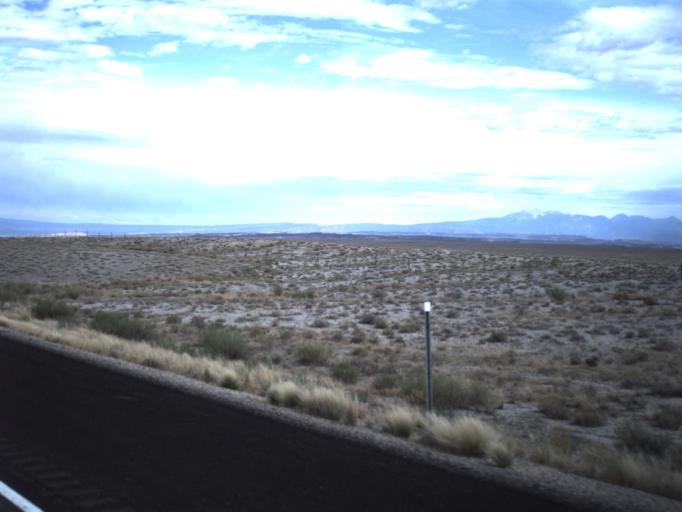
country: US
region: Utah
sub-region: Grand County
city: Moab
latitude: 38.9419
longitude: -109.6265
